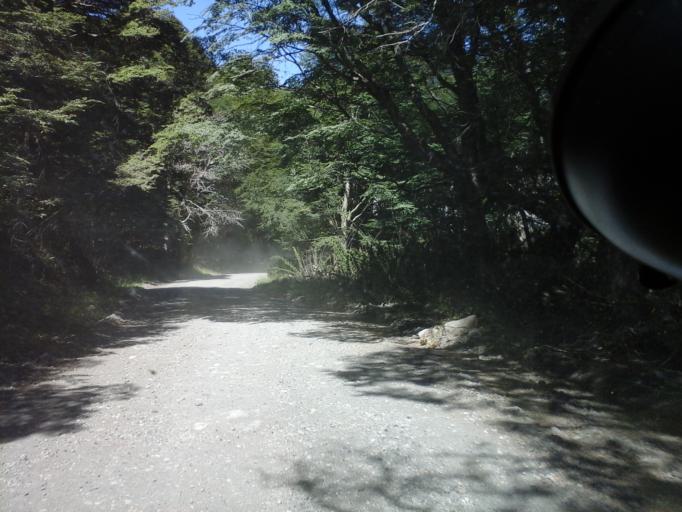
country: AR
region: Neuquen
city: Villa La Angostura
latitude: -41.2105
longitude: -71.8105
